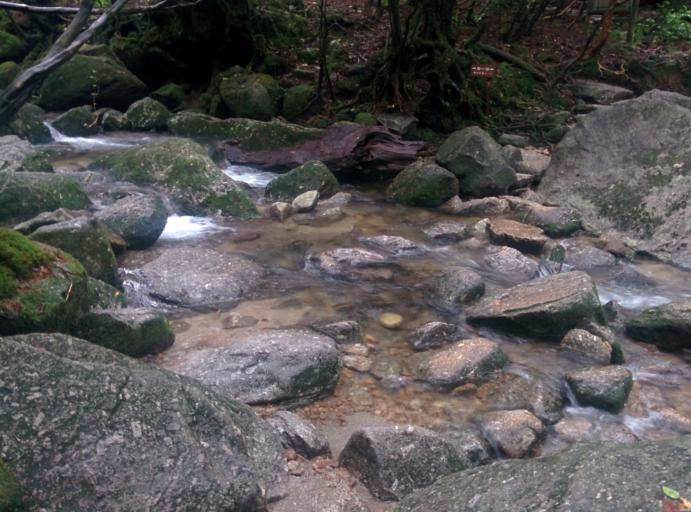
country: JP
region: Kagoshima
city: Nishinoomote
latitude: 30.3720
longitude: 130.5706
